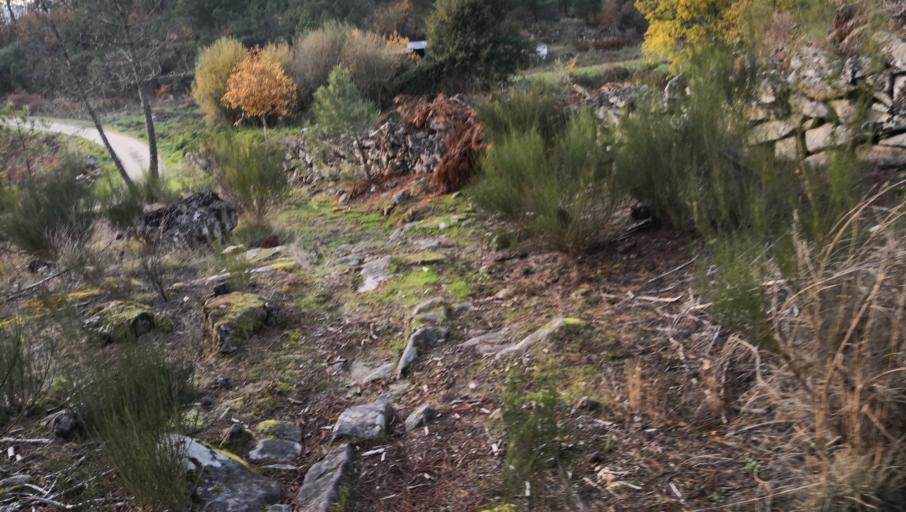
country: PT
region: Vila Real
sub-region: Vila Real
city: Vila Real
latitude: 41.3344
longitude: -7.7041
